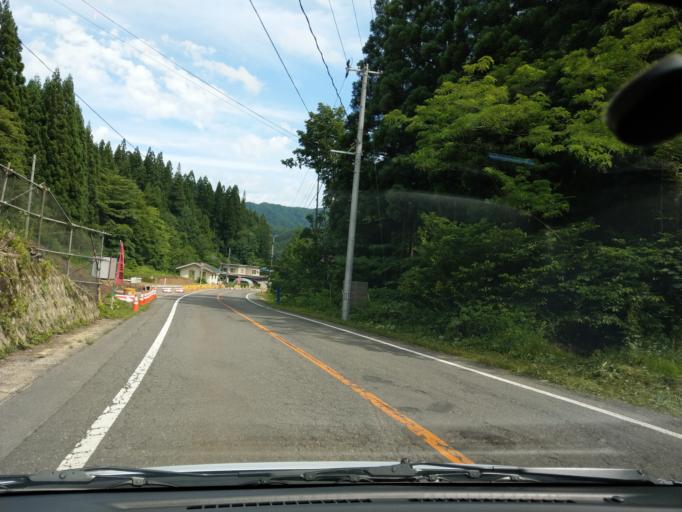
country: JP
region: Akita
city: Kakunodatemachi
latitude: 39.7297
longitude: 140.5838
